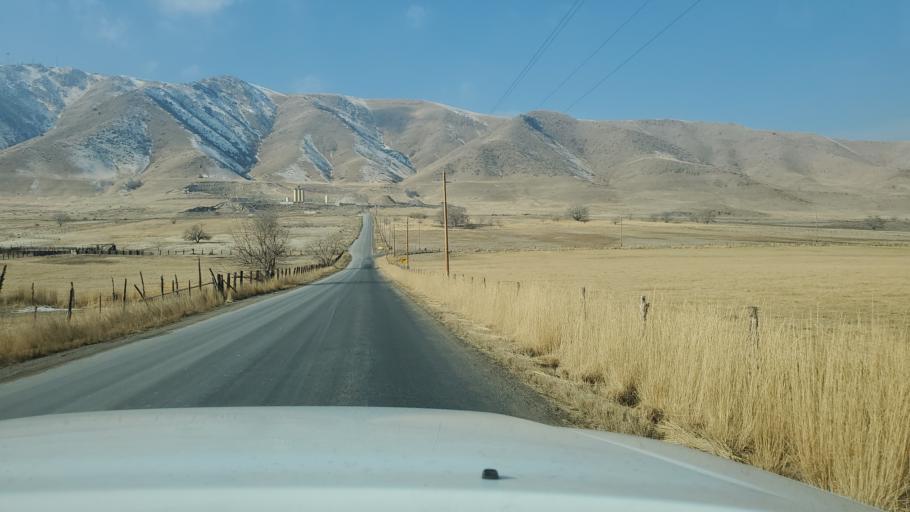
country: US
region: Utah
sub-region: Utah County
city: West Mountain
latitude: 40.0997
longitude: -111.7944
